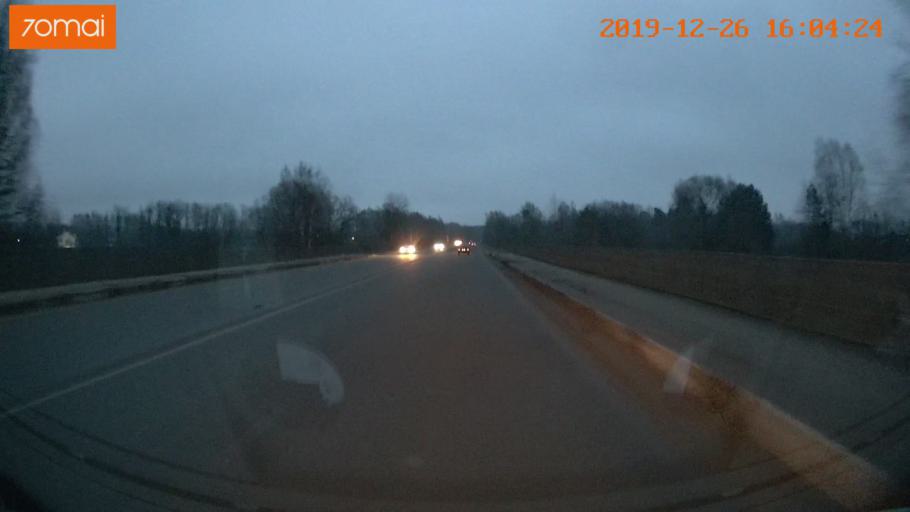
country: RU
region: Jaroslavl
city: Rybinsk
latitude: 58.0084
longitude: 38.8694
